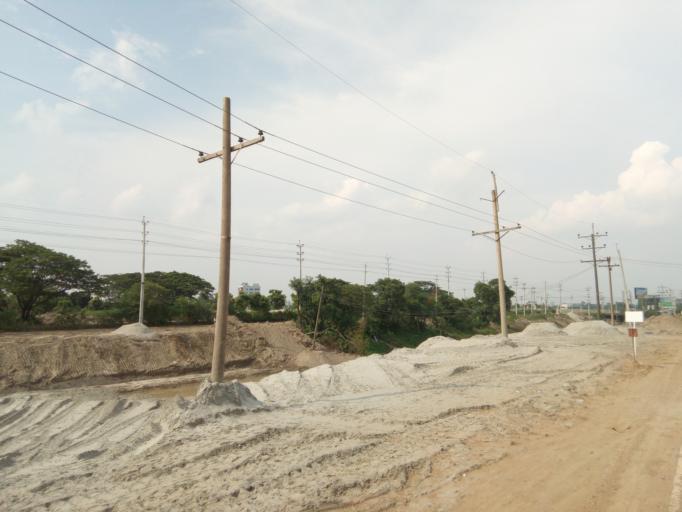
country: BD
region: Dhaka
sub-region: Dhaka
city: Dhaka
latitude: 23.6731
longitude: 90.4030
